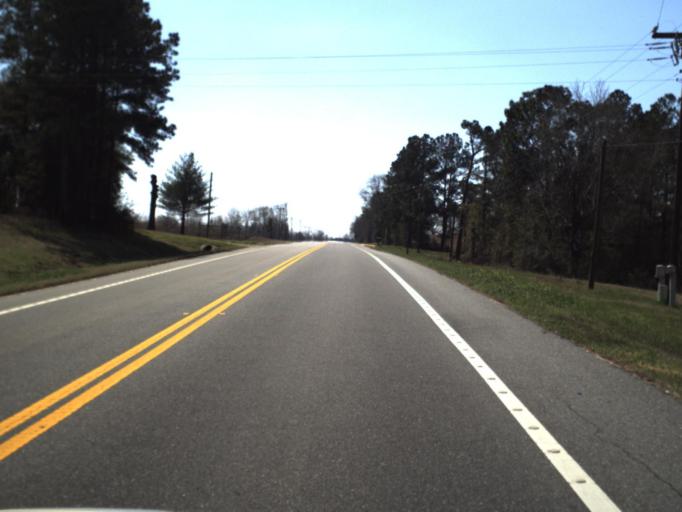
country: US
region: Florida
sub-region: Jackson County
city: Sneads
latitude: 30.6839
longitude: -85.0279
